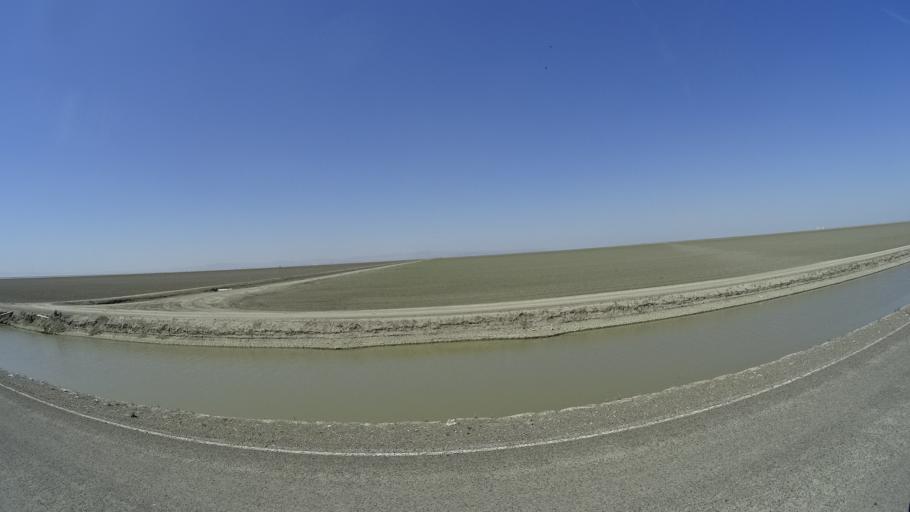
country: US
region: California
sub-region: Kings County
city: Corcoran
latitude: 35.9709
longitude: -119.6432
